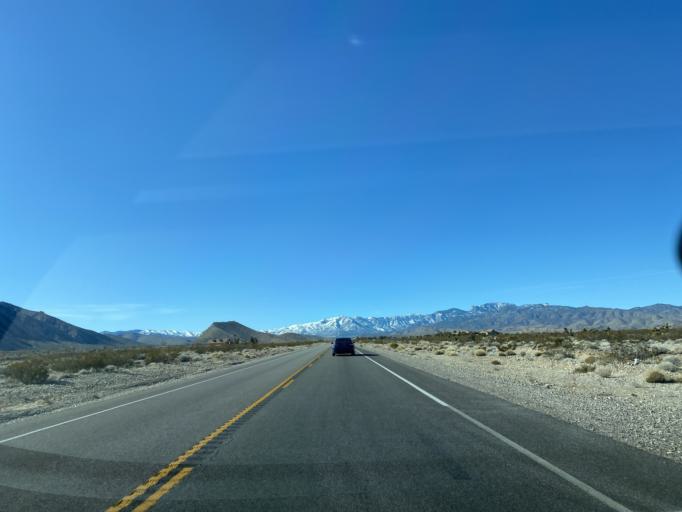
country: US
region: Nevada
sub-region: Clark County
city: Summerlin South
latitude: 36.3181
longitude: -115.3652
